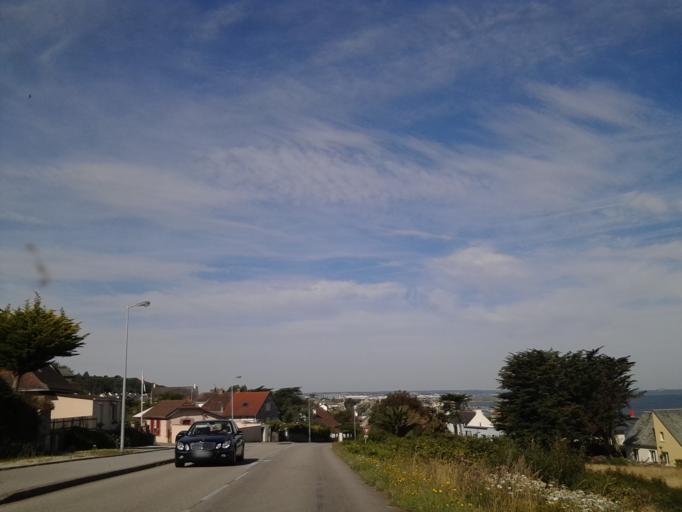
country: FR
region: Lower Normandy
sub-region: Departement de la Manche
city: Bretteville
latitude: 49.6536
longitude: -1.5386
